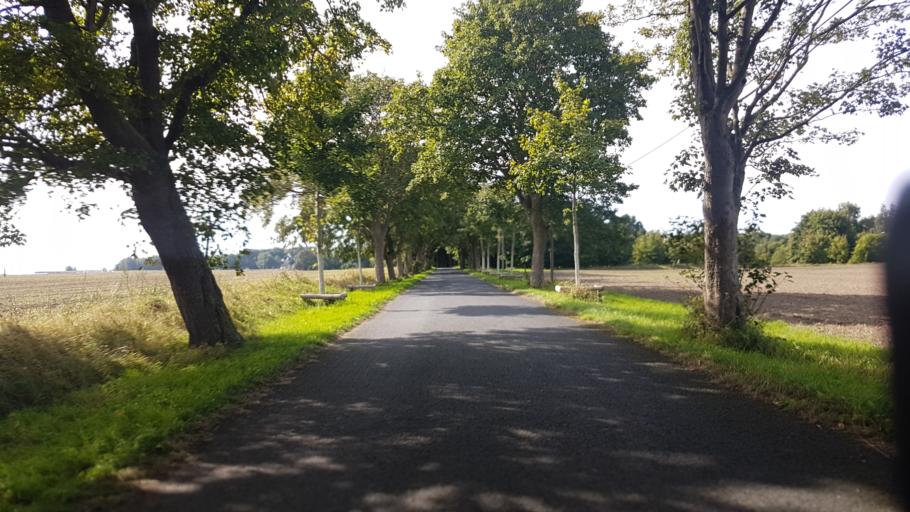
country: DE
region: Mecklenburg-Vorpommern
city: Gingst
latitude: 54.4348
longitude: 13.2166
